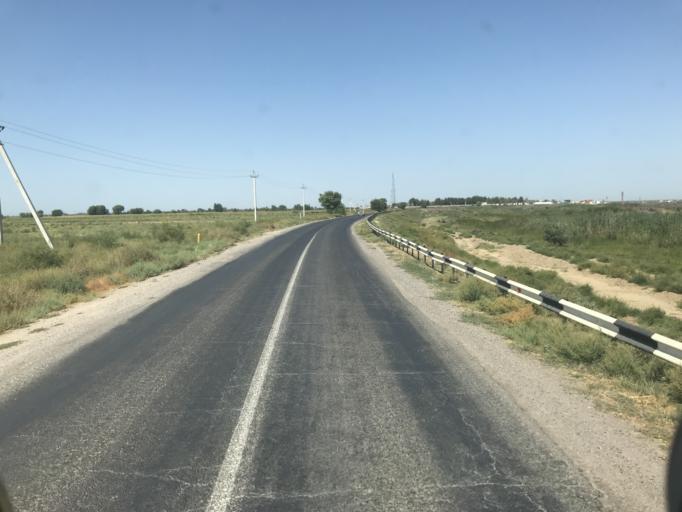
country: KZ
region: Ongtustik Qazaqstan
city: Ilyich
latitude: 40.9507
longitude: 68.4751
